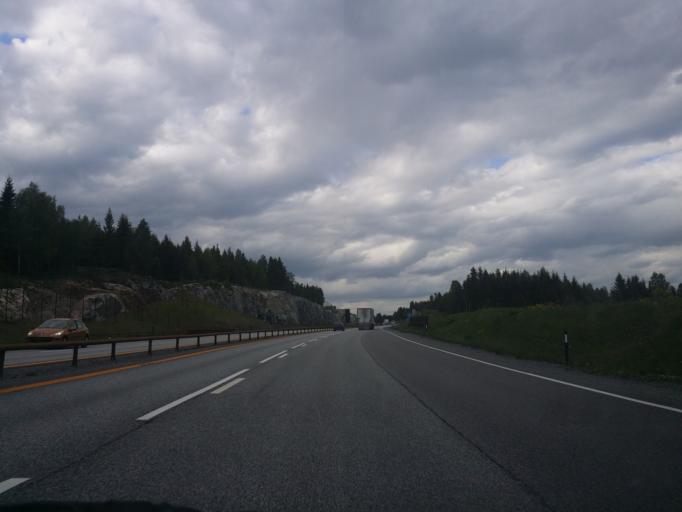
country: NO
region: Akershus
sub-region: Eidsvoll
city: Raholt
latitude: 60.2910
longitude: 11.1340
